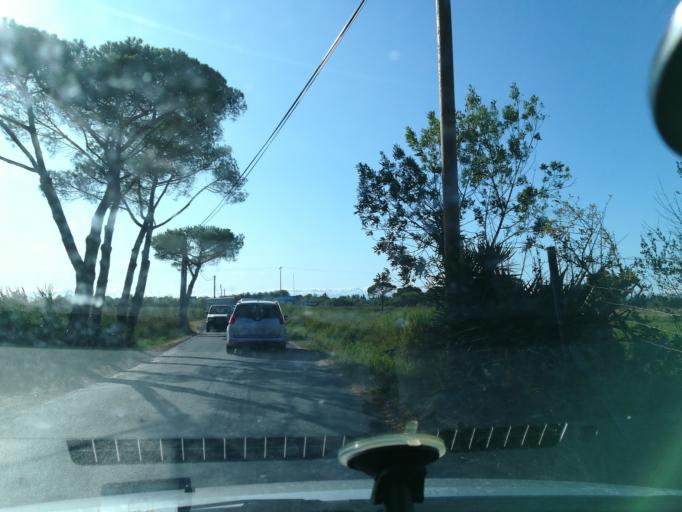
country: FR
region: Languedoc-Roussillon
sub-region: Departement de l'Herault
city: Portiragnes
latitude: 43.2876
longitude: 3.3705
